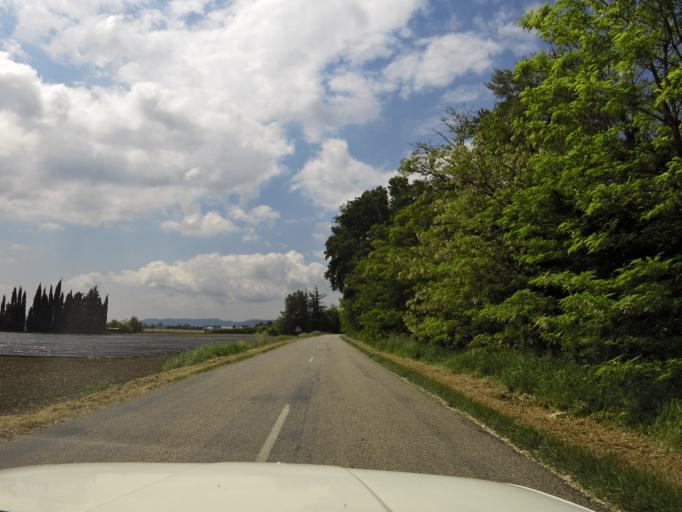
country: FR
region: Rhone-Alpes
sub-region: Departement de la Drome
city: Ancone
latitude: 44.5882
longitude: 4.7410
